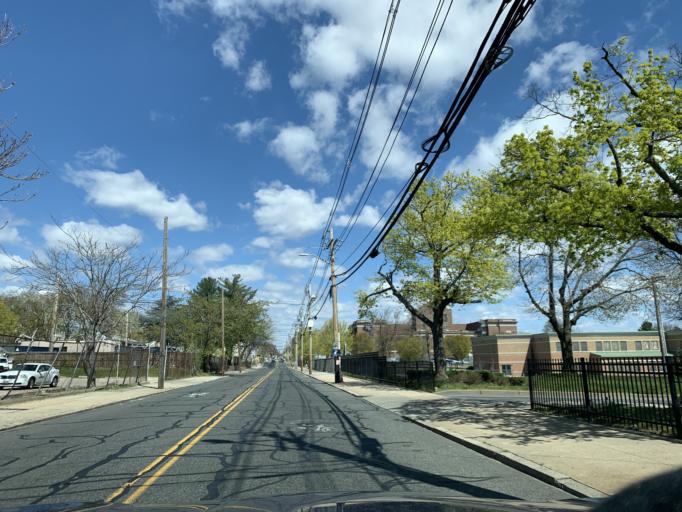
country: US
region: Rhode Island
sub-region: Providence County
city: Providence
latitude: 41.7957
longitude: -71.4106
